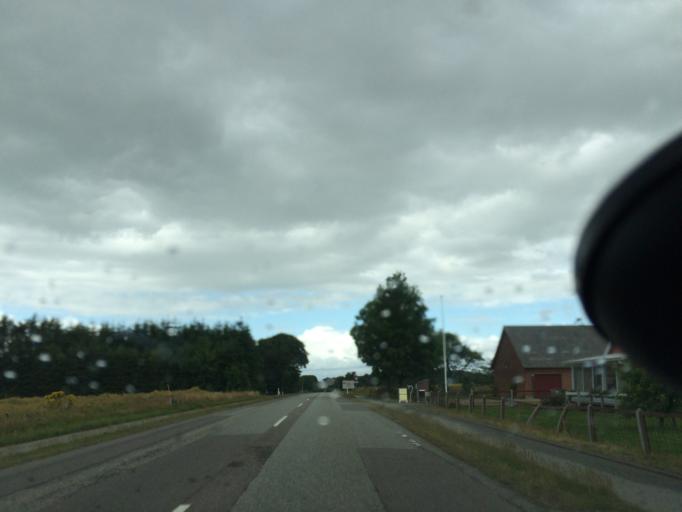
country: DK
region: Central Jutland
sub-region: Skanderborg Kommune
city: Ry
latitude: 56.1487
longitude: 9.8253
